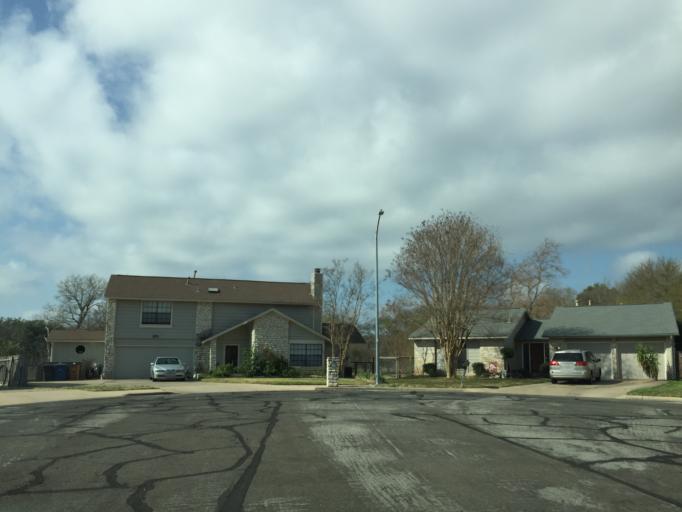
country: US
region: Texas
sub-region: Williamson County
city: Jollyville
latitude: 30.4100
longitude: -97.7350
